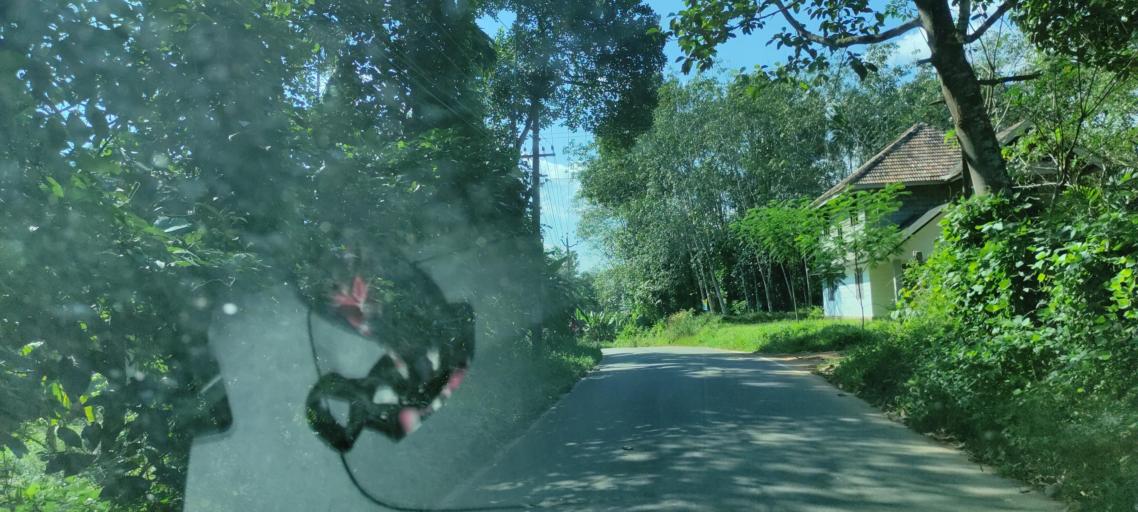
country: IN
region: Kerala
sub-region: Pattanamtitta
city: Adur
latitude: 9.2006
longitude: 76.7502
